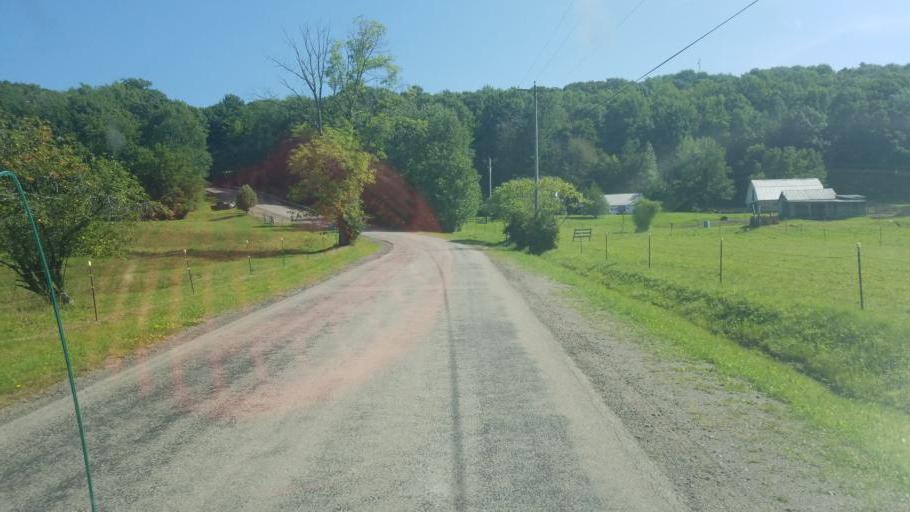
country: US
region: New York
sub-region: Allegany County
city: Bolivar
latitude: 42.0678
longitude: -78.0597
